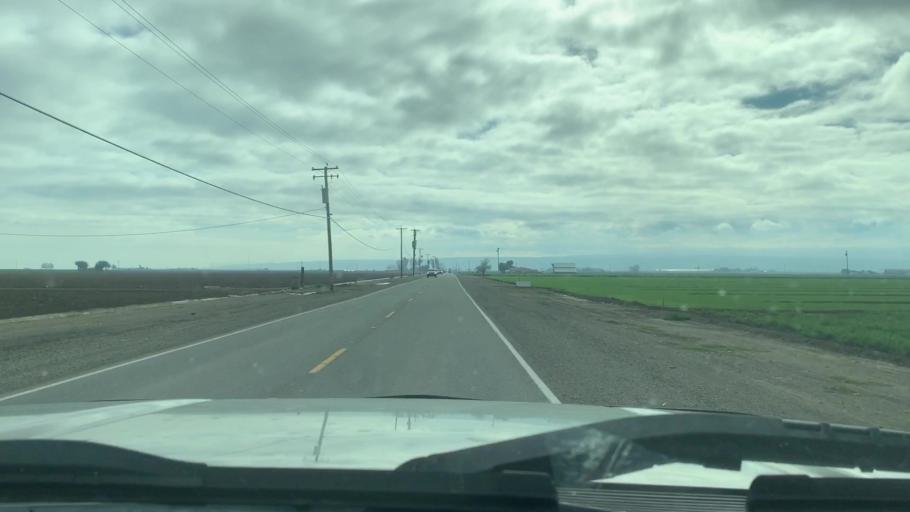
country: US
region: California
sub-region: Merced County
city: Los Banos
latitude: 37.0063
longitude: -120.8370
